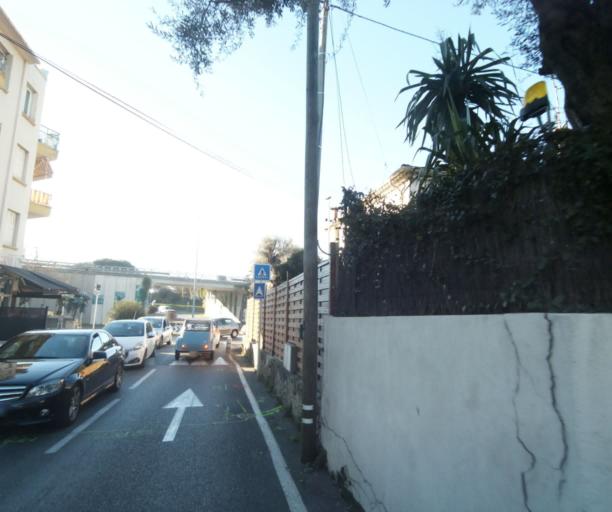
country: FR
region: Provence-Alpes-Cote d'Azur
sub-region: Departement des Alpes-Maritimes
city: Antibes
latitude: 43.5784
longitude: 7.1056
